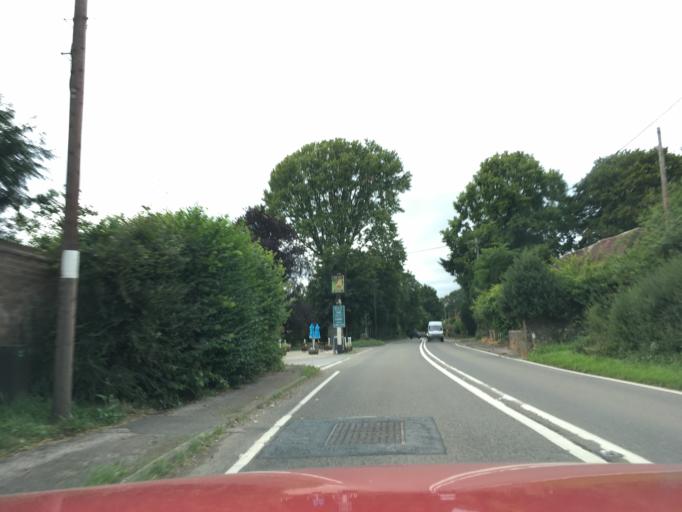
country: GB
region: England
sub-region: Hampshire
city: Four Marks
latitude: 51.0468
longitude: -1.1237
